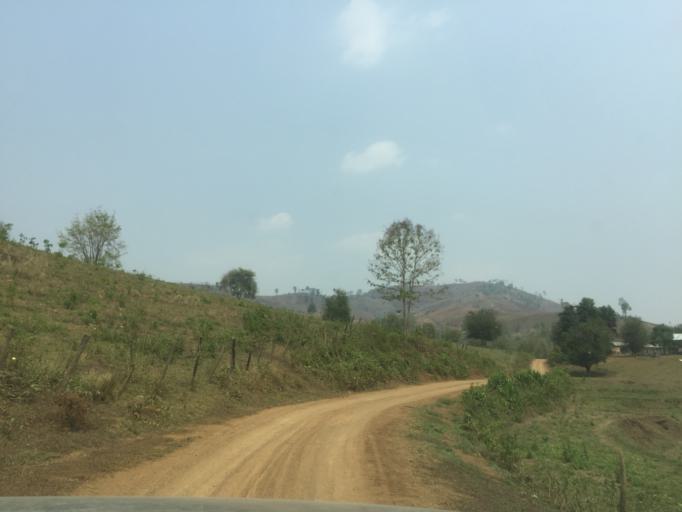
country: LA
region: Xiagnabouli
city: Muang Kenthao
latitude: 17.8110
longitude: 101.2710
